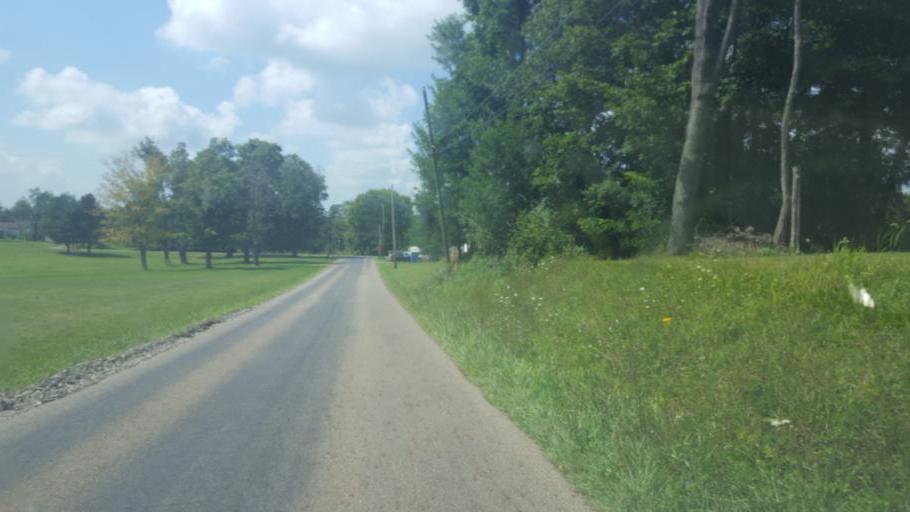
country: US
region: Ohio
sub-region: Knox County
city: Mount Vernon
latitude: 40.4193
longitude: -82.4866
